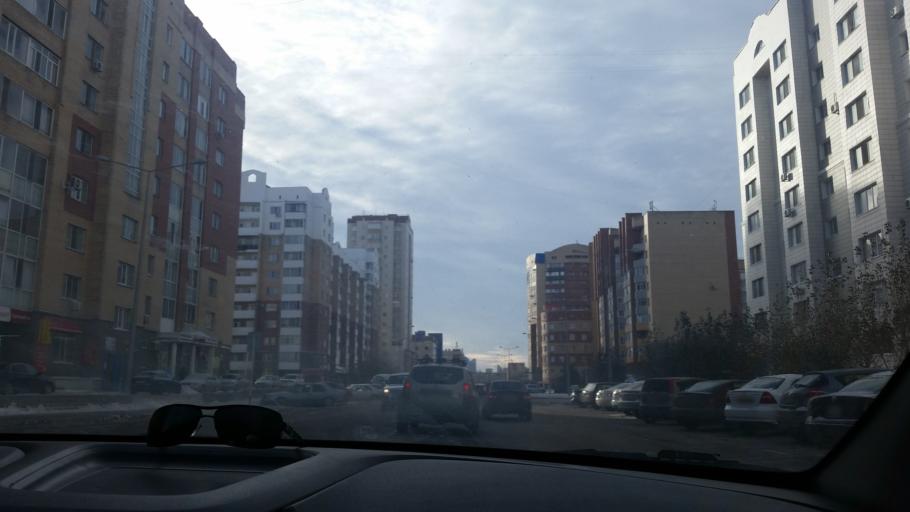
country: KZ
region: Astana Qalasy
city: Astana
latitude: 51.1487
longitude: 71.4802
